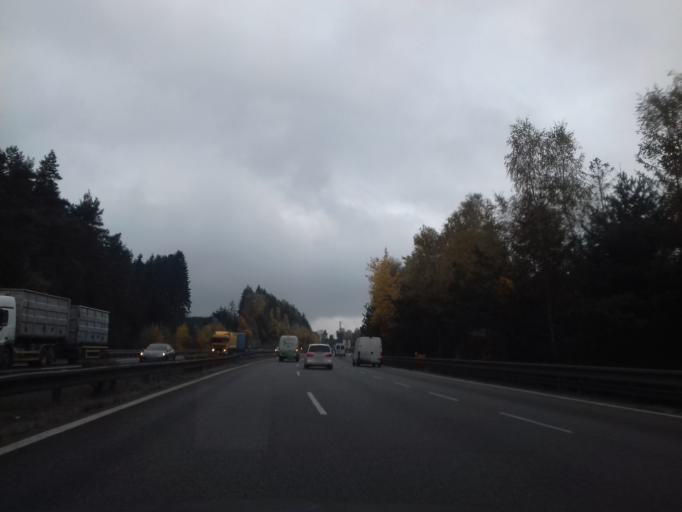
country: CZ
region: Vysocina
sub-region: Okres Pelhrimov
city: Zeliv
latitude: 49.5970
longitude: 15.2009
